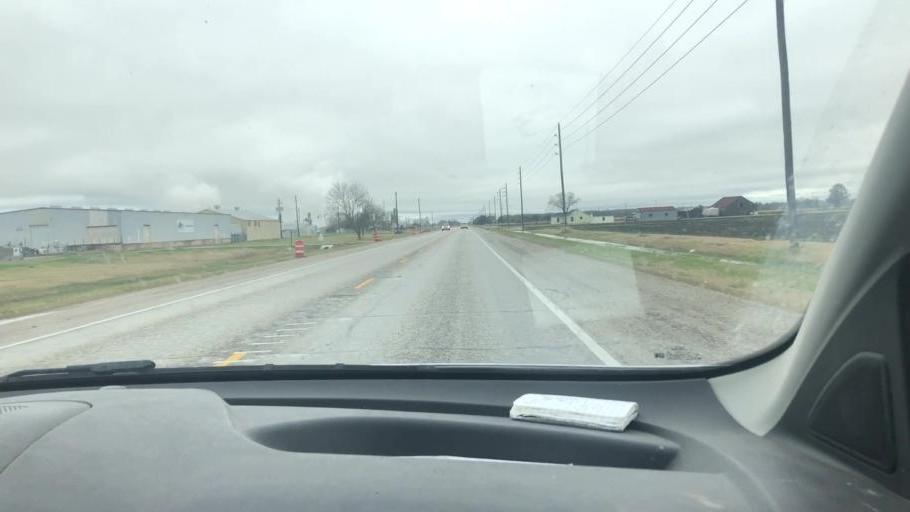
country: US
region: Texas
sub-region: Wharton County
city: Wharton
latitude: 29.2996
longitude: -96.0777
